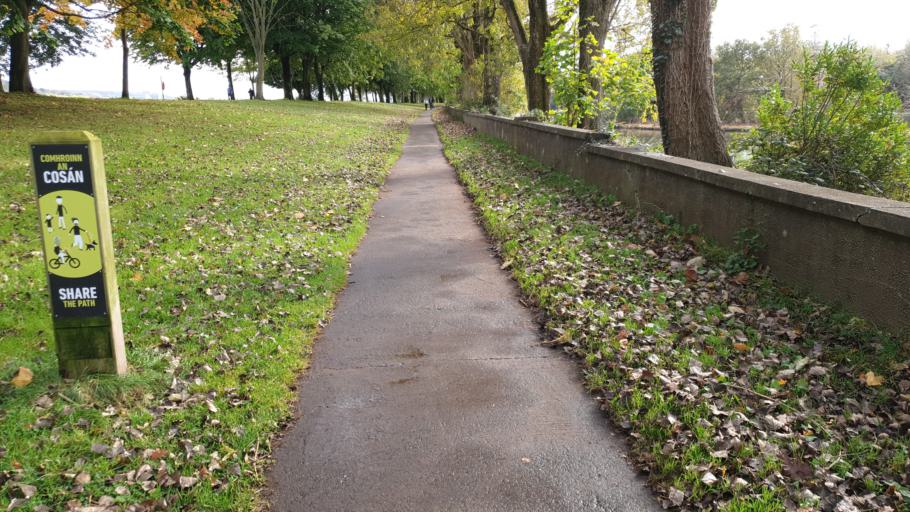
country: IE
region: Munster
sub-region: County Cork
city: Cork
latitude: 51.9006
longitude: -8.4333
